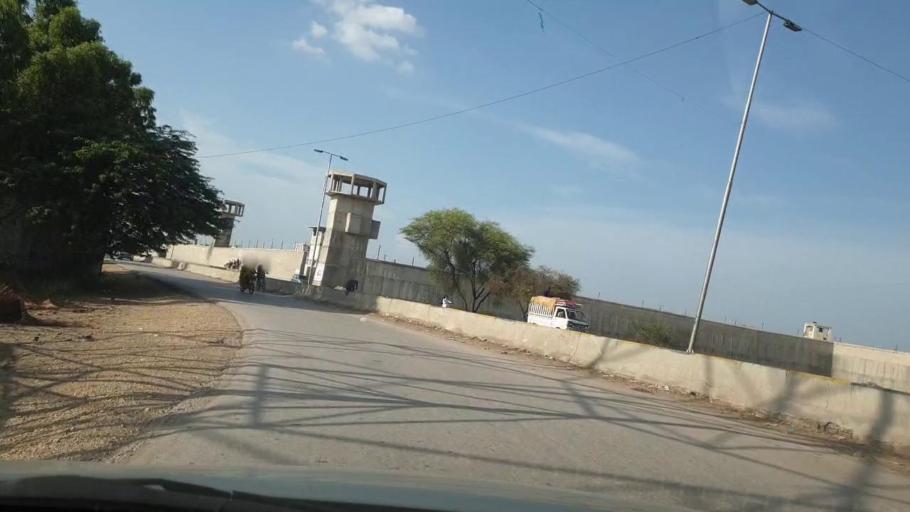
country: PK
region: Sindh
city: Sukkur
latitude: 27.6641
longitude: 68.8467
